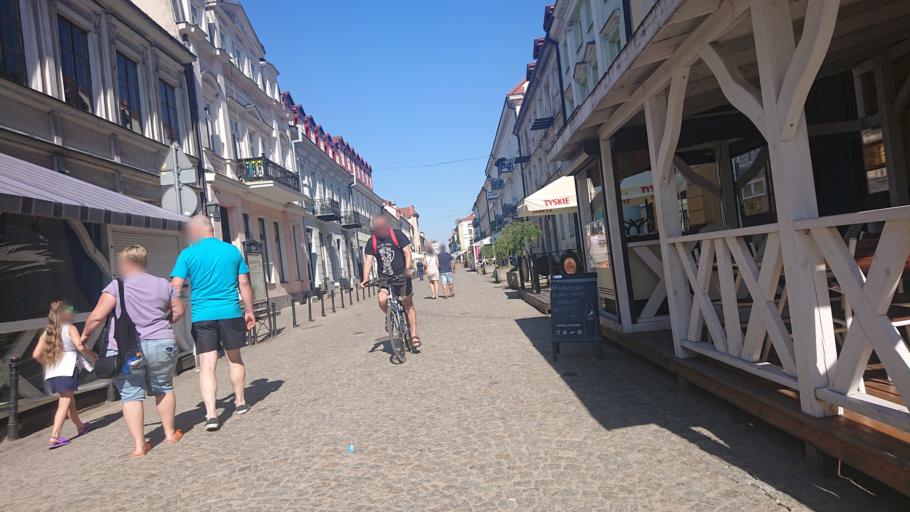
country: PL
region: Masovian Voivodeship
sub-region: Plock
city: Plock
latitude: 52.5435
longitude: 19.6883
